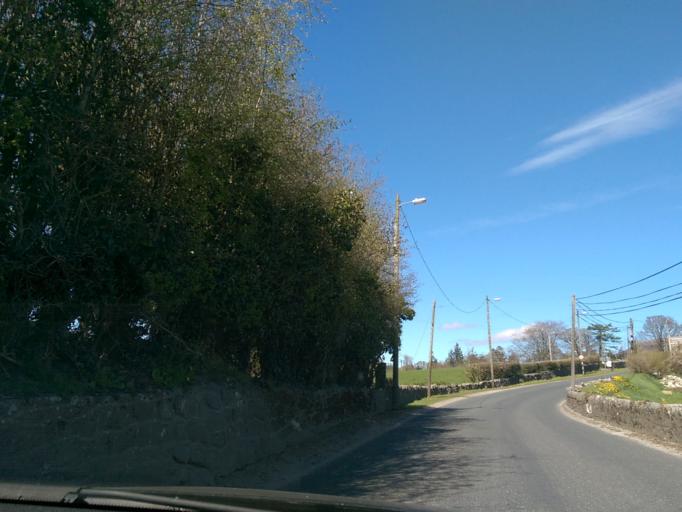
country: IE
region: Leinster
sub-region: Wicklow
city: Baltinglass
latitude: 52.9017
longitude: -6.6085
